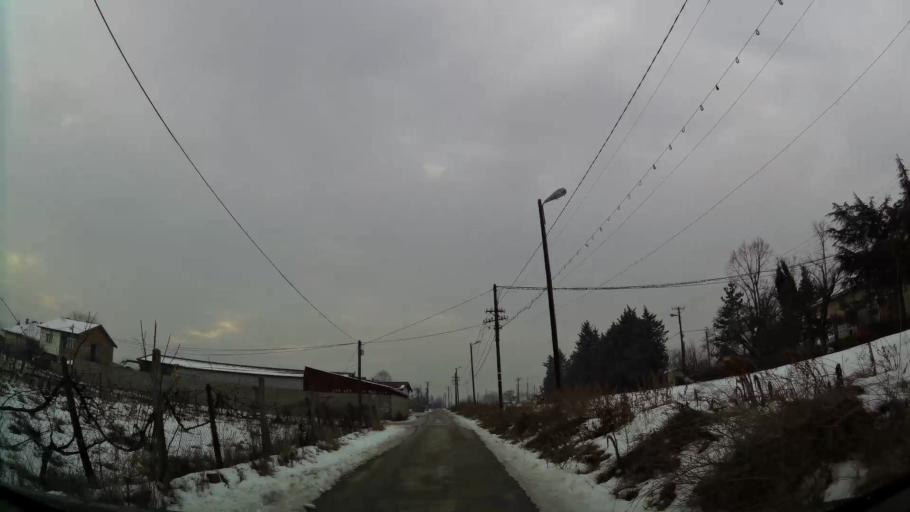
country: MK
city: Kondovo
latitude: 42.0472
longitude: 21.3542
